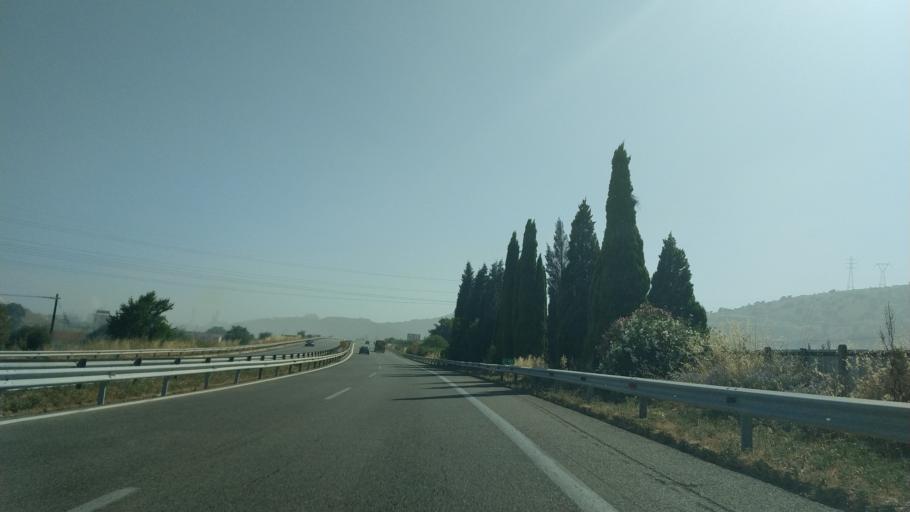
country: GR
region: East Macedonia and Thrace
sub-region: Nomos Kavalas
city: Nea Karvali
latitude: 40.9687
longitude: 24.4892
